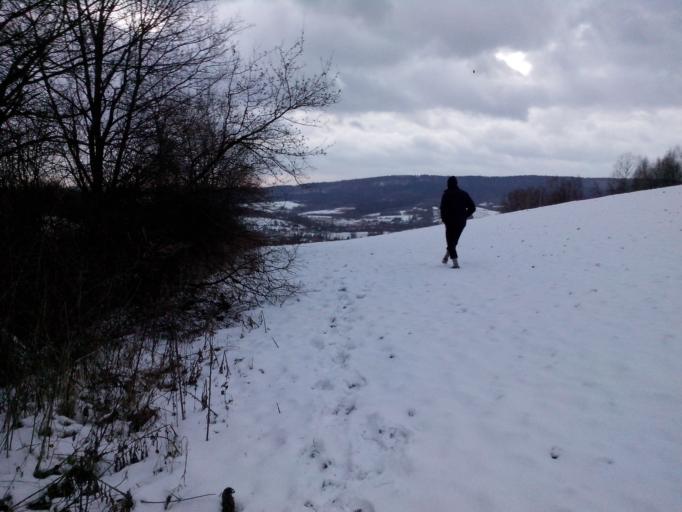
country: PL
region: Subcarpathian Voivodeship
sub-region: Powiat strzyzowski
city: Jawornik
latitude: 49.8419
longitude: 21.8433
